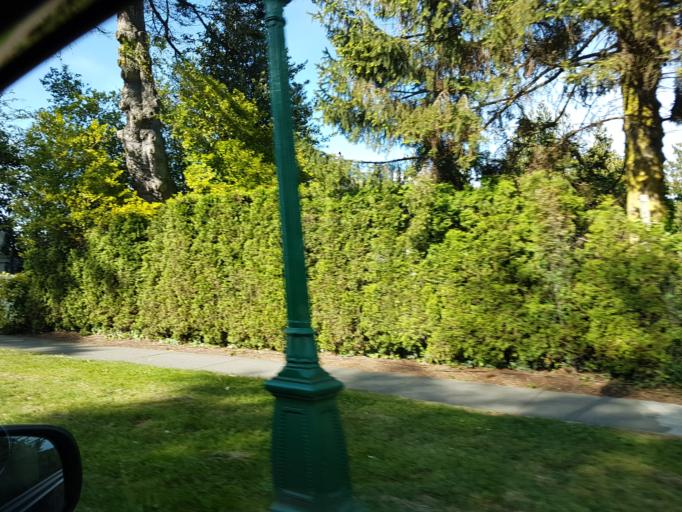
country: CA
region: British Columbia
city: Oak Bay
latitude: 48.4489
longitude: -123.2950
